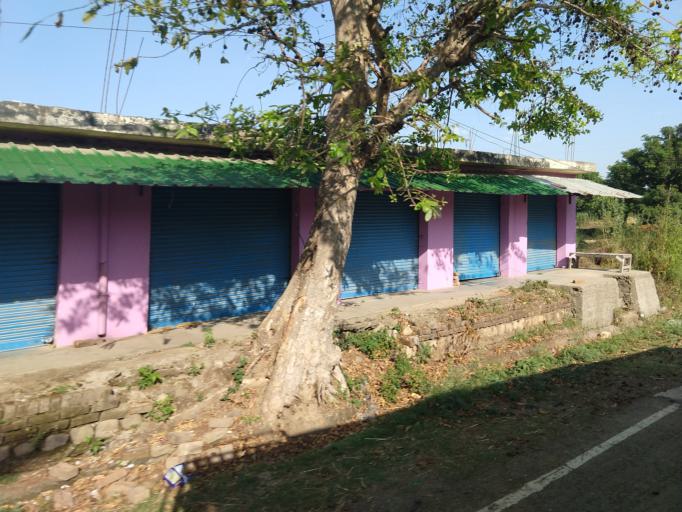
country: IN
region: Himachal Pradesh
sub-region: Chamba
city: Chowari
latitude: 32.3607
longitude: 75.9210
